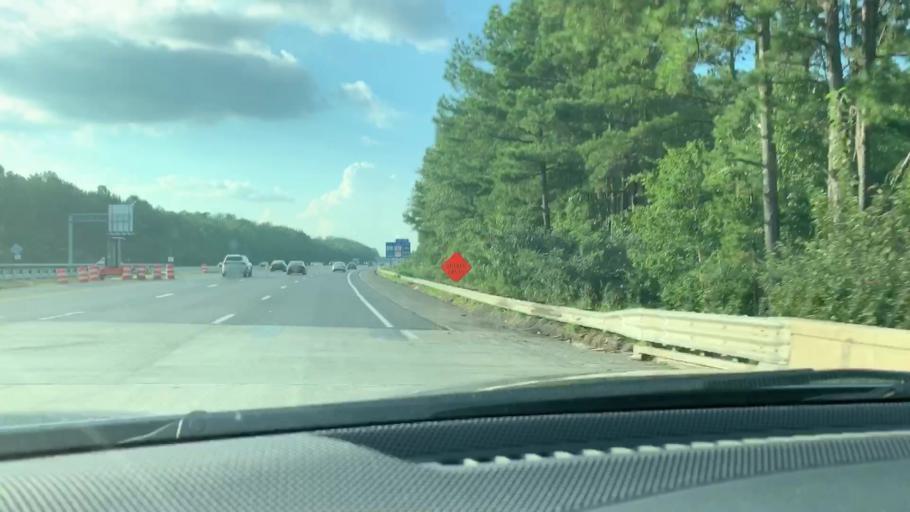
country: US
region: South Carolina
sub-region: Richland County
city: Woodfield
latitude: 34.0741
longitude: -80.9297
